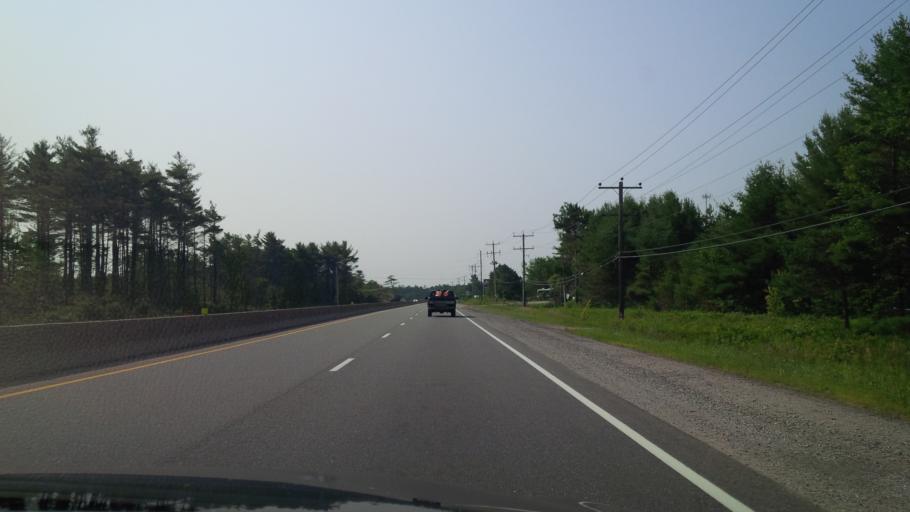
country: CA
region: Ontario
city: Gravenhurst
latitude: 44.8703
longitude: -79.3267
